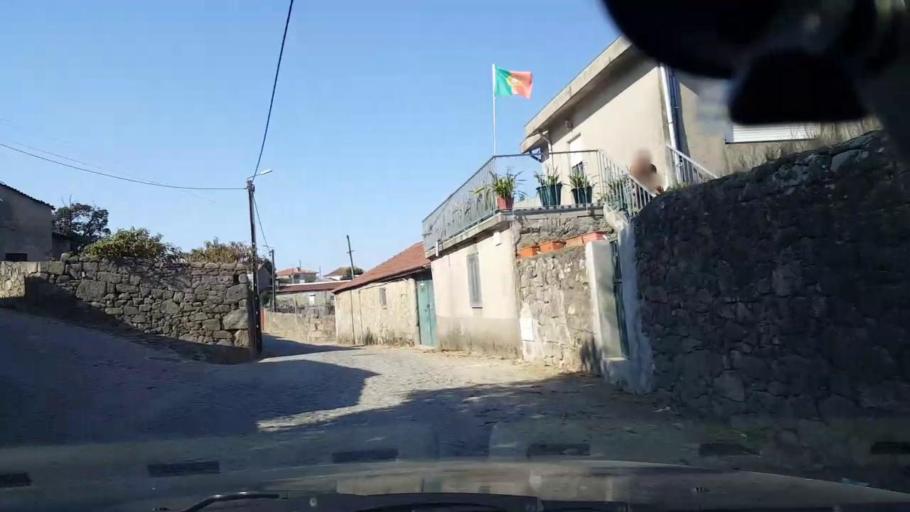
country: PT
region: Porto
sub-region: Vila do Conde
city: Arvore
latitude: 41.3619
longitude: -8.6966
